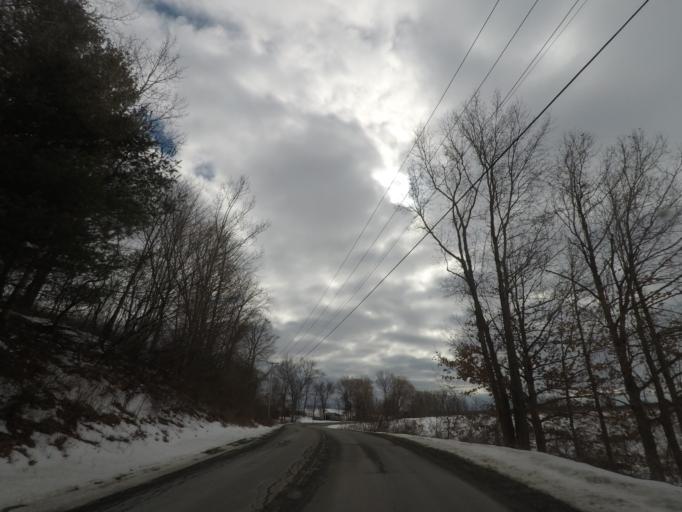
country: US
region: New York
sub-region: Rensselaer County
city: Hoosick Falls
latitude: 42.9251
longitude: -73.4350
